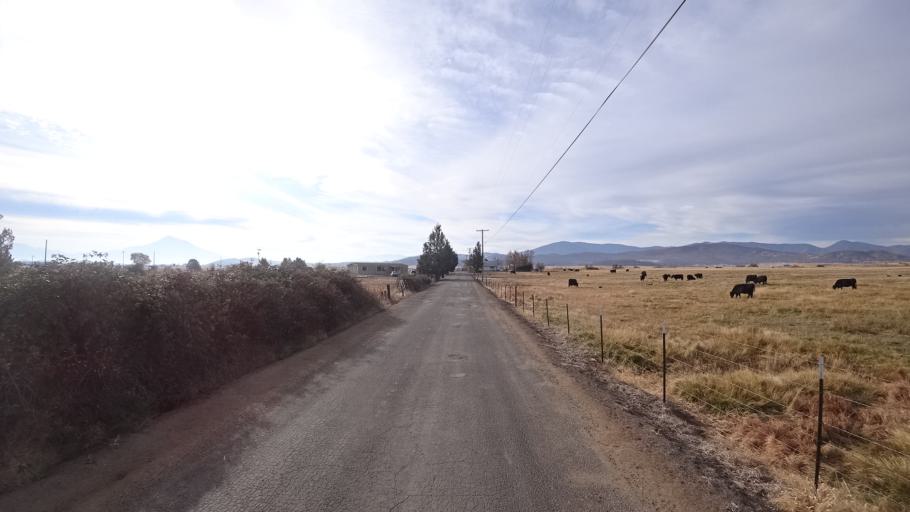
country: US
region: California
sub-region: Siskiyou County
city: Montague
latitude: 41.7268
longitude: -122.5786
